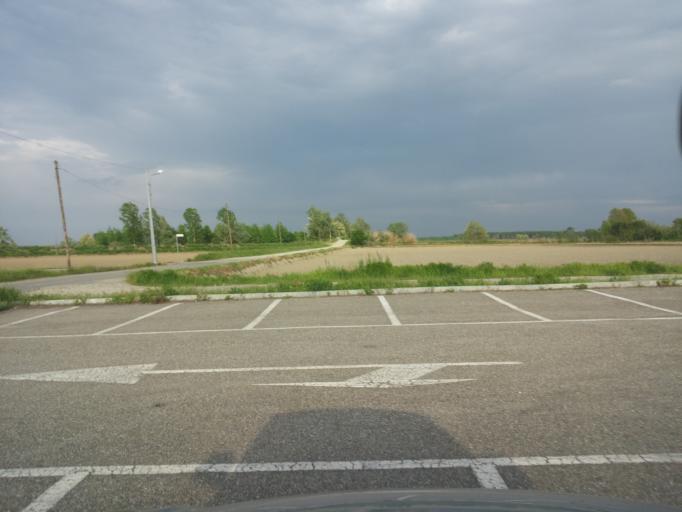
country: IT
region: Piedmont
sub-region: Provincia di Vercelli
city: Motta De Conti
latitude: 45.1926
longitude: 8.5254
